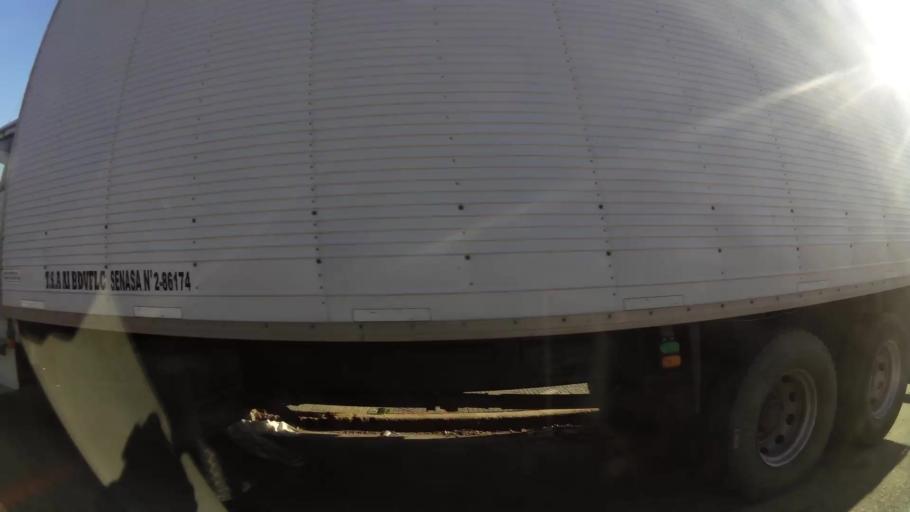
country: AR
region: Cordoba
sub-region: Departamento de Capital
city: Cordoba
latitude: -31.3806
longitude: -64.1858
